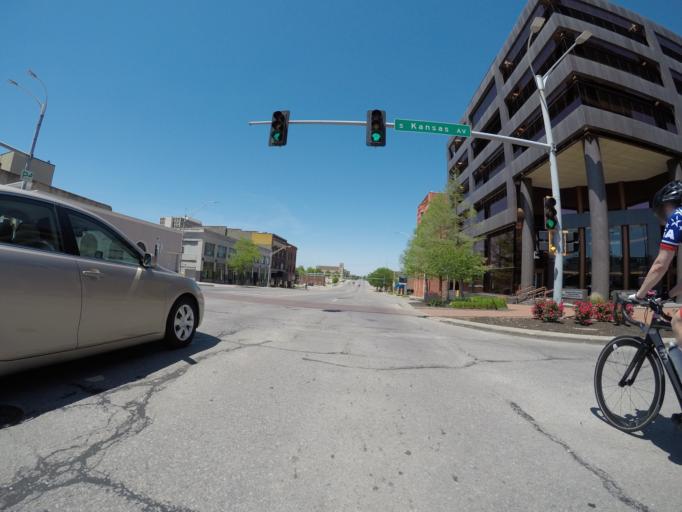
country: US
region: Kansas
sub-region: Shawnee County
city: Topeka
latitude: 39.0519
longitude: -95.6732
